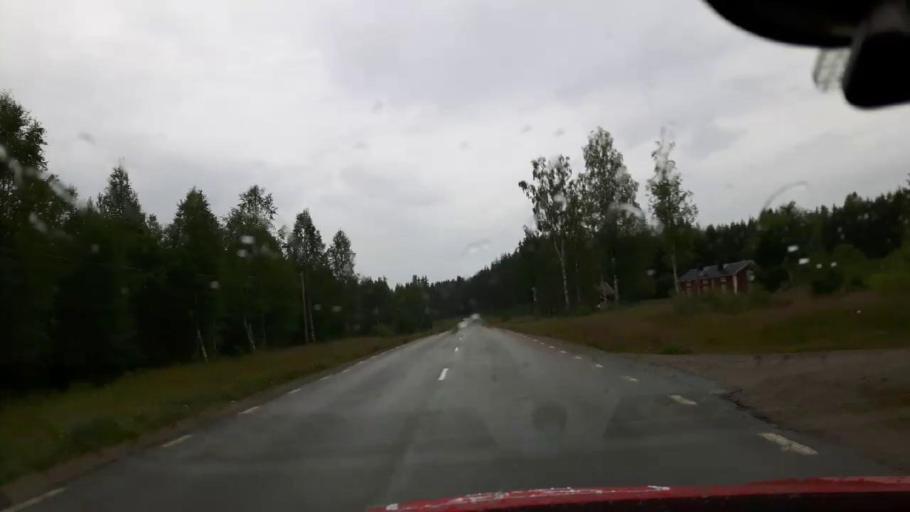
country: SE
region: Jaemtland
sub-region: OEstersunds Kommun
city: Brunflo
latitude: 62.8374
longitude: 15.0074
